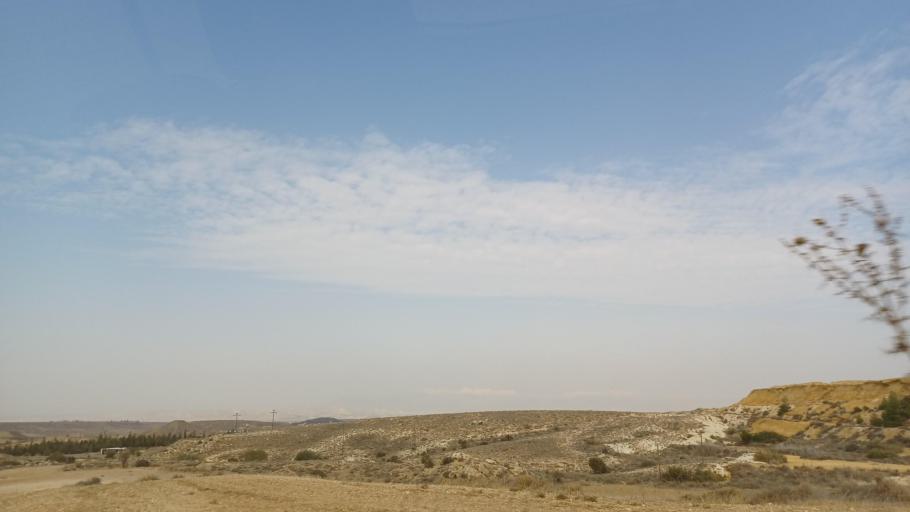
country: CY
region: Lefkosia
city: Meniko
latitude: 35.0670
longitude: 33.1213
